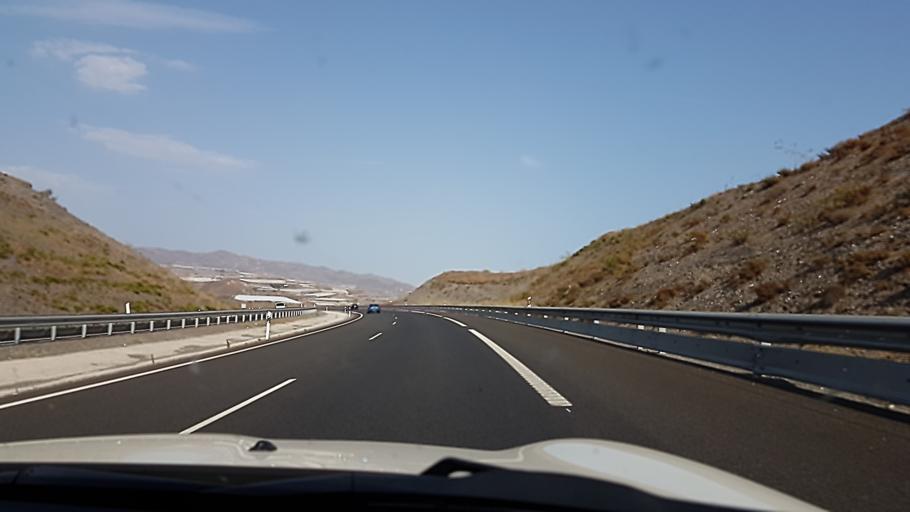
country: ES
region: Andalusia
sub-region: Provincia de Granada
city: Albunol
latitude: 36.7505
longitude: -3.2119
